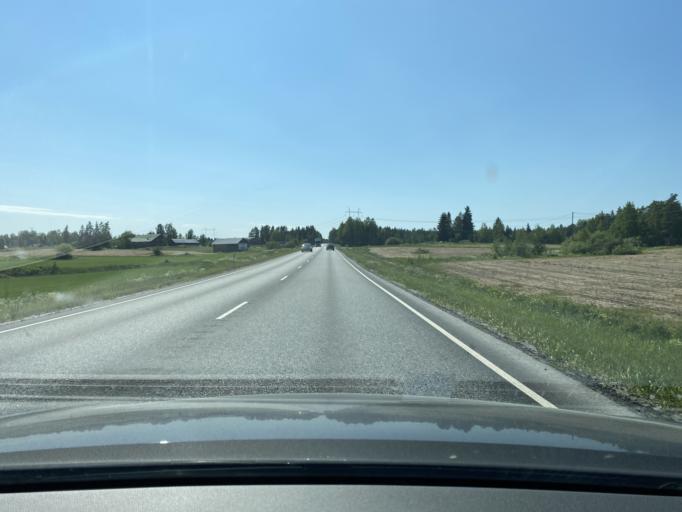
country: FI
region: Pirkanmaa
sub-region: Tampere
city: Nokia
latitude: 61.4178
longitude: 23.3229
